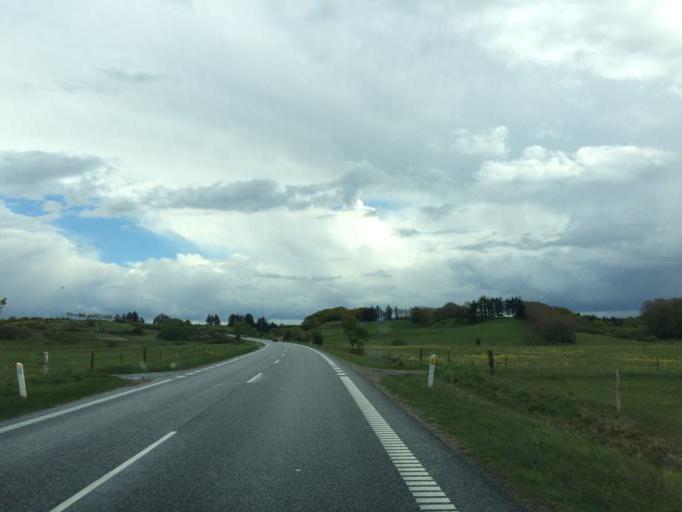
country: DK
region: Central Jutland
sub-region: Skive Kommune
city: Hojslev
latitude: 56.6045
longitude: 9.2998
